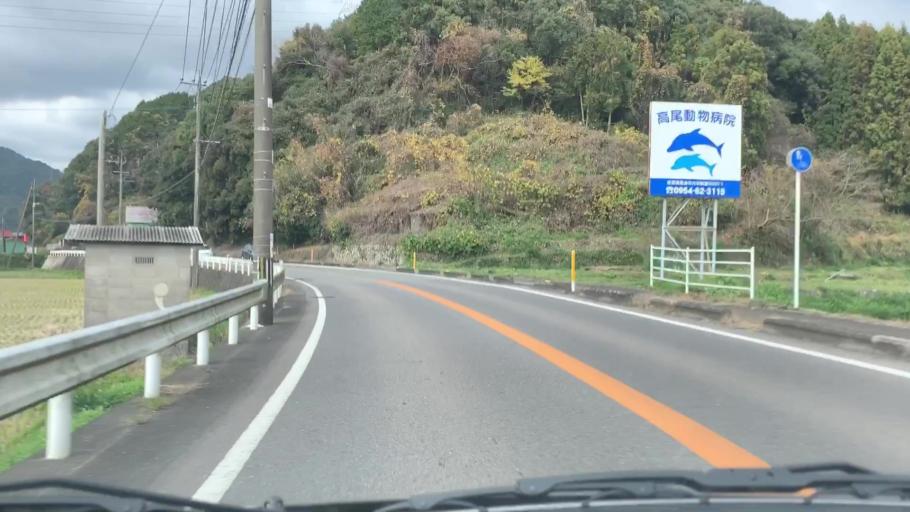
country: JP
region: Saga Prefecture
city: Ureshinomachi-shimojuku
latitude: 33.1344
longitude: 130.0292
